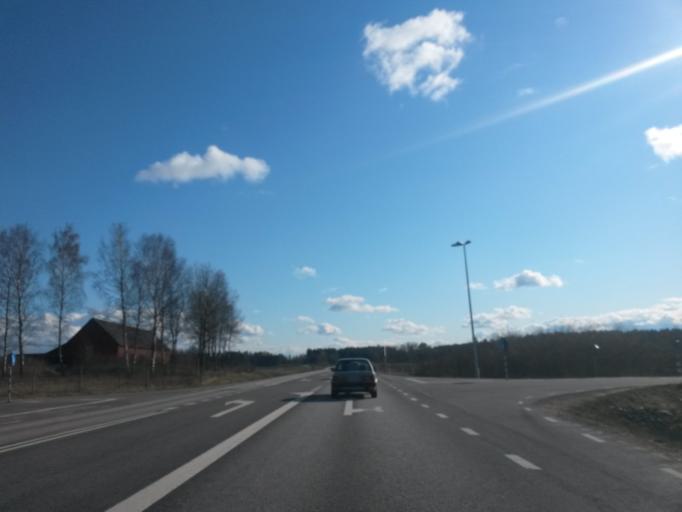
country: SE
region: Vaestra Goetaland
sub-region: Vara Kommun
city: Vara
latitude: 58.1712
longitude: 12.8889
